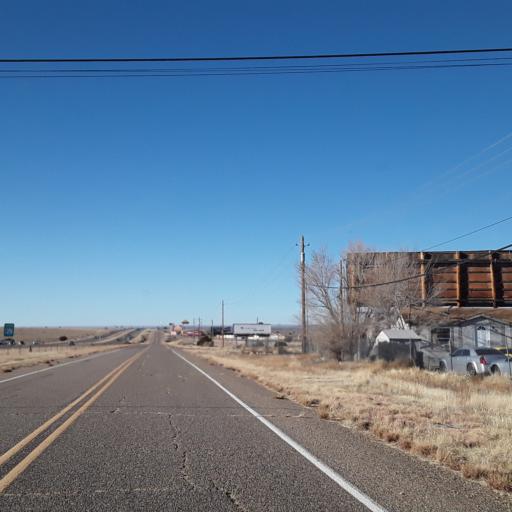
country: US
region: New Mexico
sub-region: Sandoval County
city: Santo Domingo Pueblo
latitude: 35.4575
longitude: -106.3366
